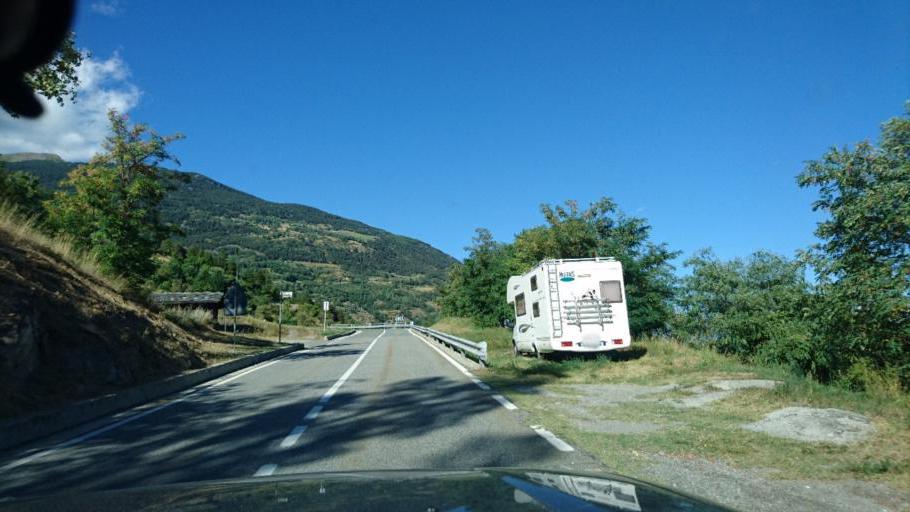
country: IT
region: Aosta Valley
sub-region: Valle d'Aosta
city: Villeneuve
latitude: 45.7096
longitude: 7.2075
